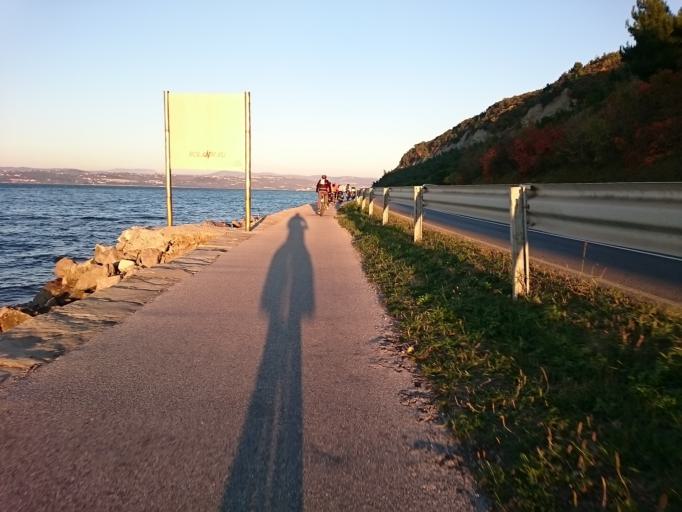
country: SI
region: Izola-Isola
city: Izola
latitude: 45.5456
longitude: 13.6799
